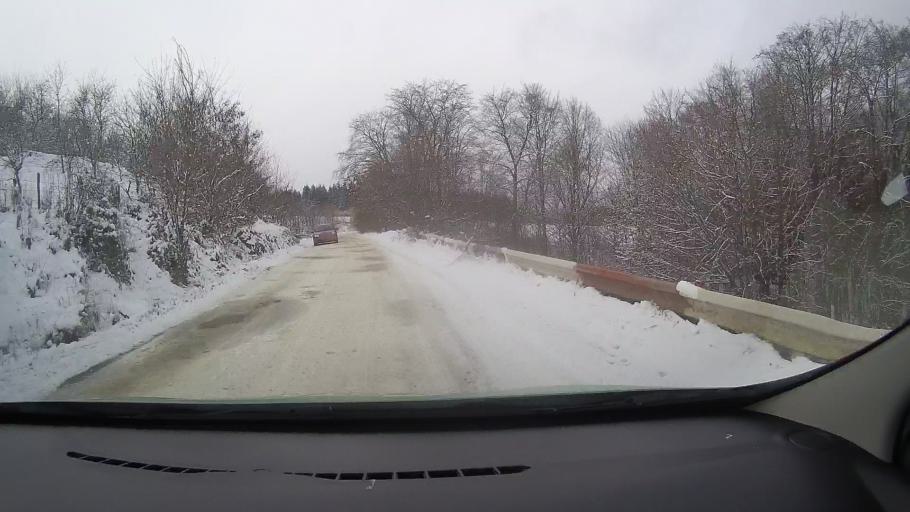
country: RO
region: Alba
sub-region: Comuna Almasu Mare
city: Almasu Mare
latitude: 46.0961
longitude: 23.1612
